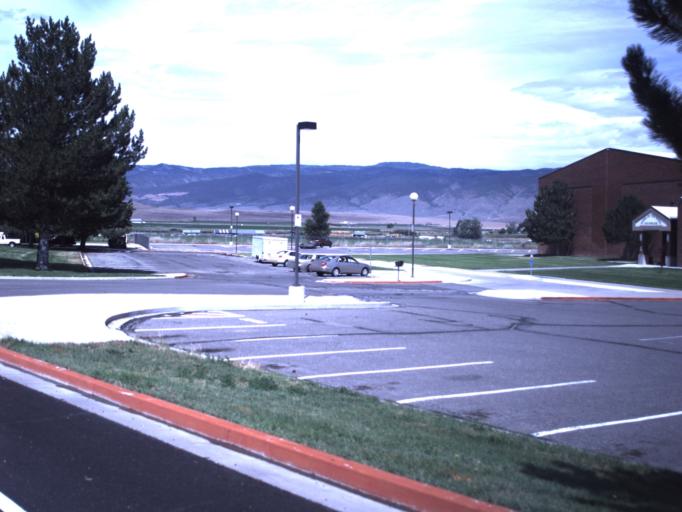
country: US
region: Utah
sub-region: Sevier County
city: Monroe
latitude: 38.6297
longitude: -112.1308
